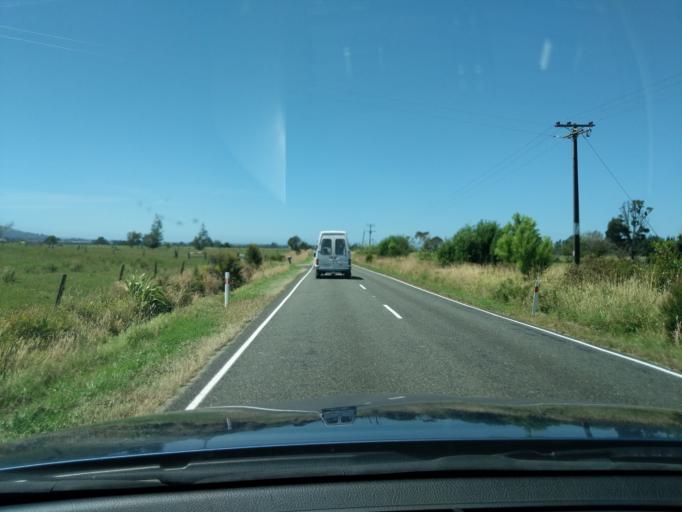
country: NZ
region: Tasman
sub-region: Tasman District
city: Takaka
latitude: -40.6904
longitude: 172.6450
